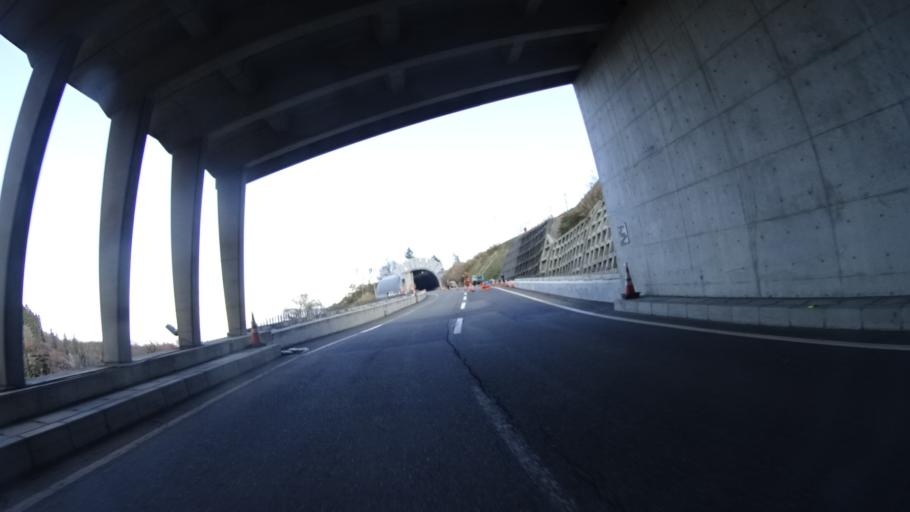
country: JP
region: Niigata
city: Shiozawa
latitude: 36.9847
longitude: 138.7798
